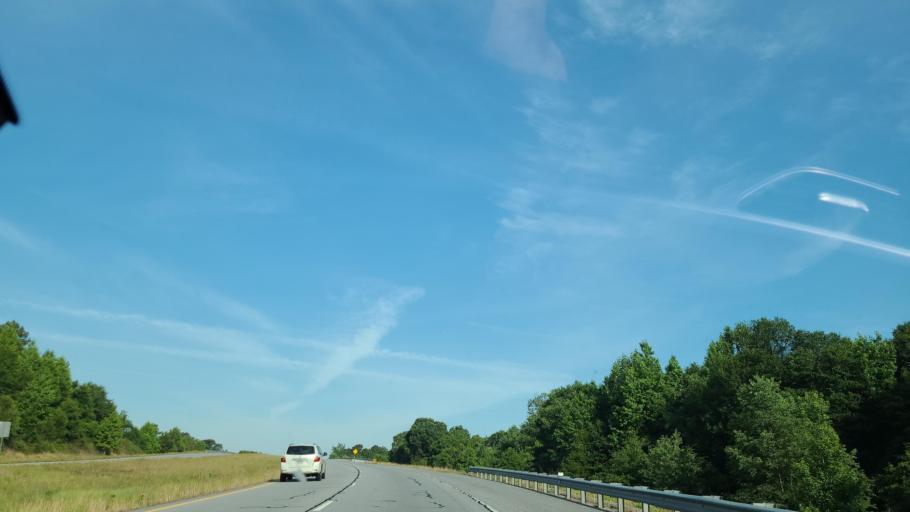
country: US
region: Georgia
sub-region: Jackson County
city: Nicholson
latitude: 34.0599
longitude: -83.4149
